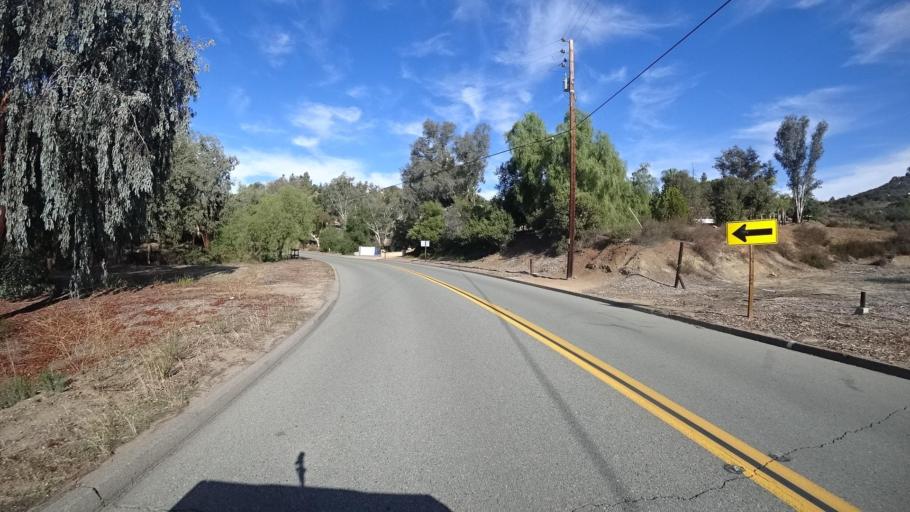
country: US
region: California
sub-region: San Diego County
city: Alpine
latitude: 32.8172
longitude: -116.7423
